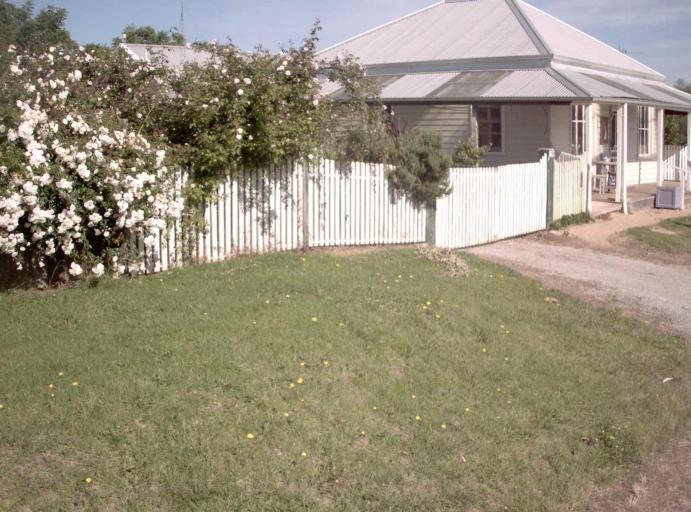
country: AU
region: Victoria
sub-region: East Gippsland
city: Bairnsdale
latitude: -37.7325
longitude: 147.8111
